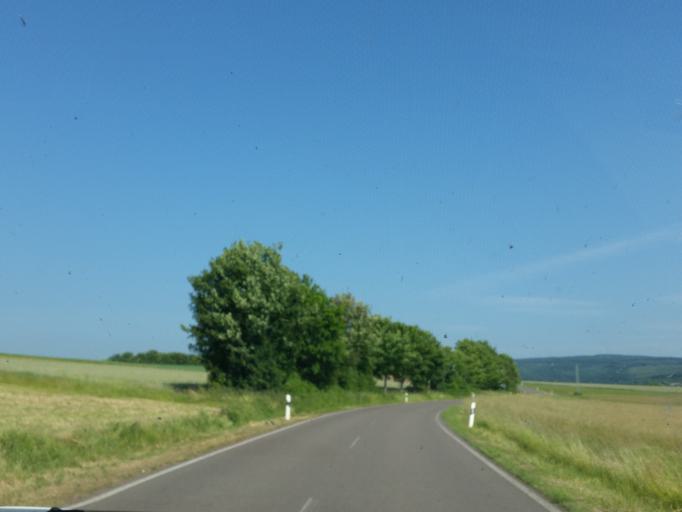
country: DE
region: Saarland
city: Weiskirchen
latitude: 49.5291
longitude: 6.8103
